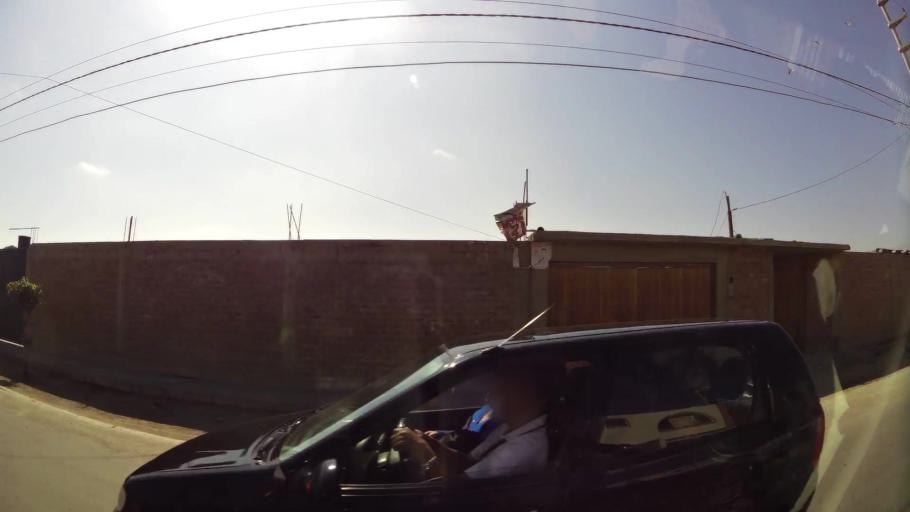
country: PE
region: Ica
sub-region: Provincia de Chincha
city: Sunampe
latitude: -13.4196
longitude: -76.1634
